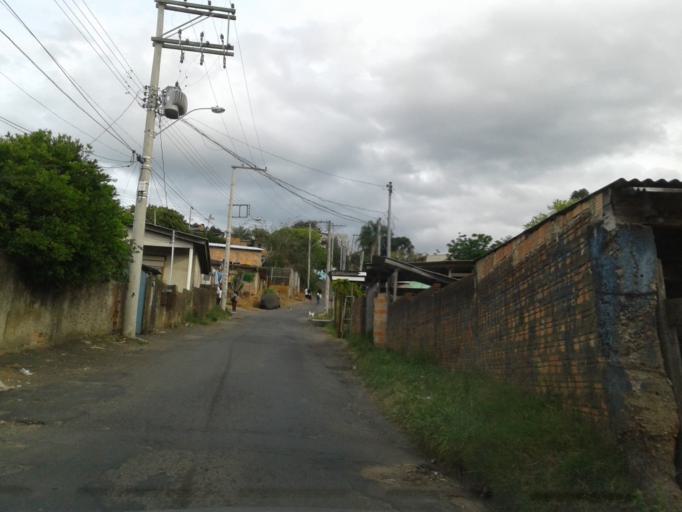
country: BR
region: Rio Grande do Sul
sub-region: Porto Alegre
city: Porto Alegre
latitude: -30.0607
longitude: -51.1460
